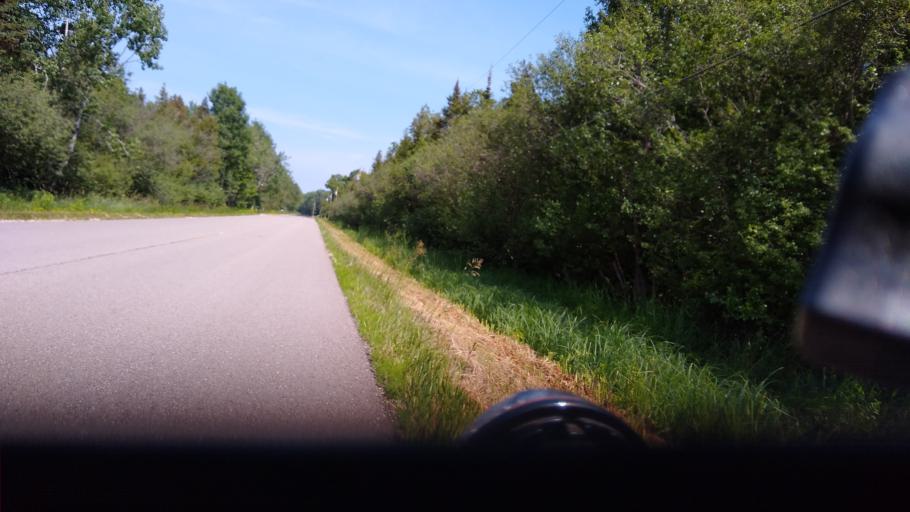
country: US
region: Michigan
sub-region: Delta County
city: Escanaba
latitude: 45.7101
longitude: -87.1065
